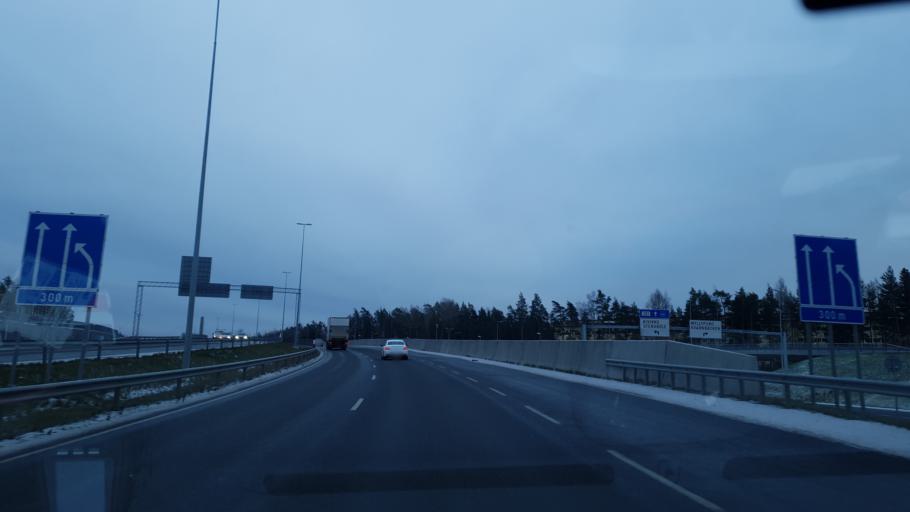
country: FI
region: Uusimaa
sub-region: Helsinki
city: Vantaa
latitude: 60.2307
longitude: 25.0529
